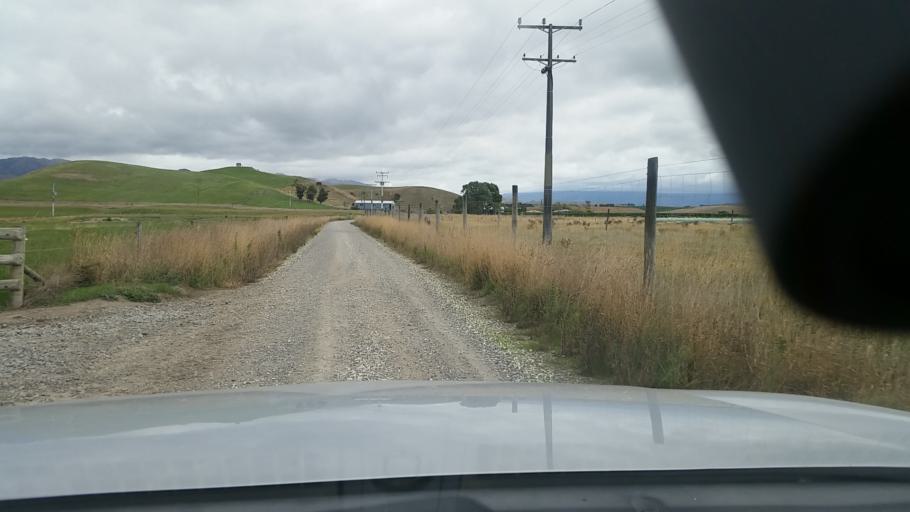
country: NZ
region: Marlborough
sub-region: Marlborough District
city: Blenheim
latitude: -41.7004
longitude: 174.1166
